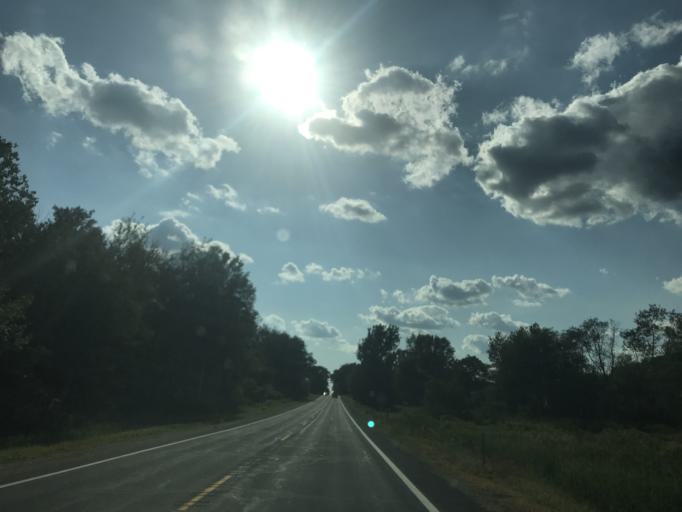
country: US
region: Michigan
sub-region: Newaygo County
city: White Cloud
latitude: 43.5685
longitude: -85.7829
